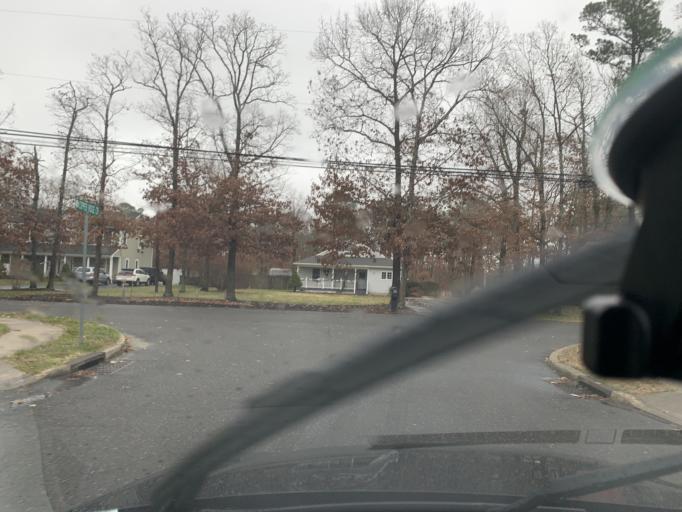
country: US
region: New Jersey
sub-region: Atlantic County
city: Pomona
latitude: 39.4278
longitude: -74.5869
